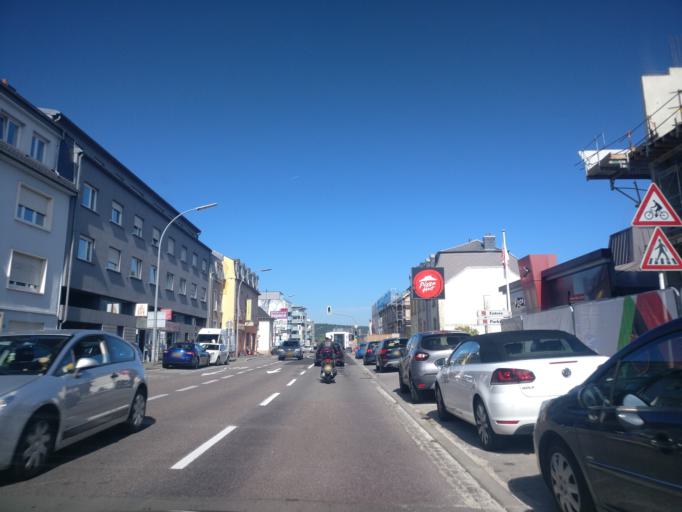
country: LU
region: Luxembourg
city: Bereldange
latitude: 49.6447
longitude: 6.1289
